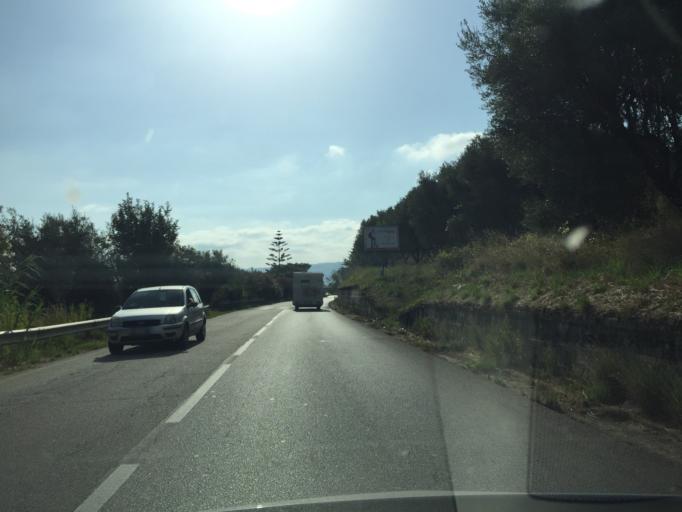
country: IT
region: Calabria
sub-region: Provincia di Vibo-Valentia
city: Pannaconi
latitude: 38.7167
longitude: 16.0543
